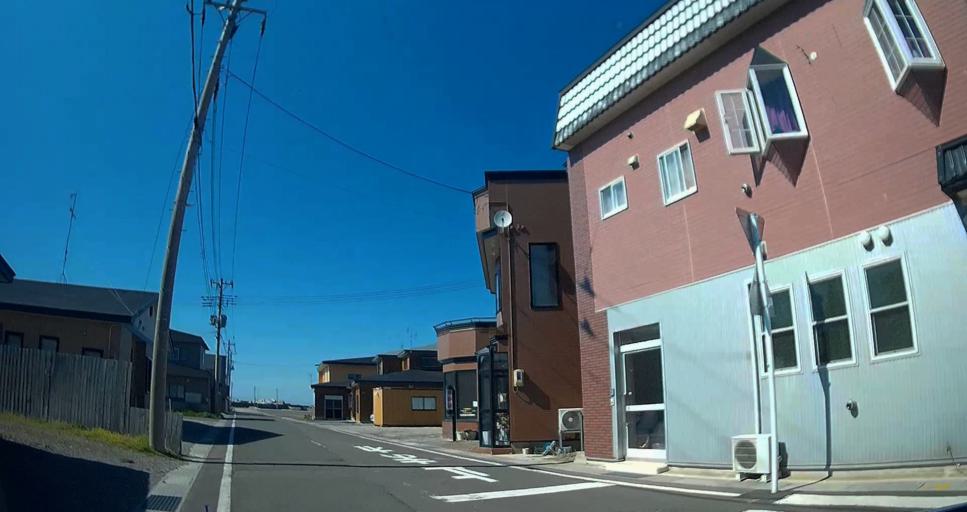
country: JP
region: Hokkaido
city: Hakodate
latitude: 41.5281
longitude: 140.9049
